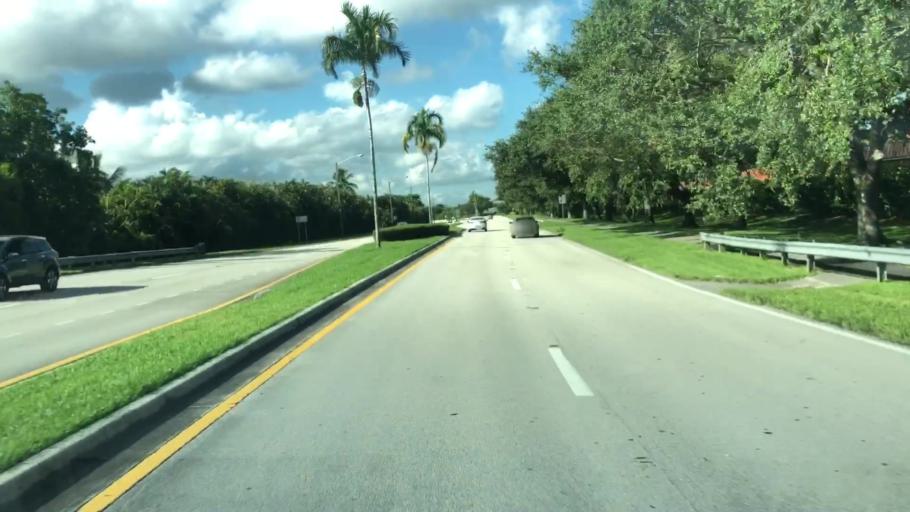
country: US
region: Florida
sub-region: Broward County
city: Tamarac
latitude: 26.2385
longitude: -80.2693
